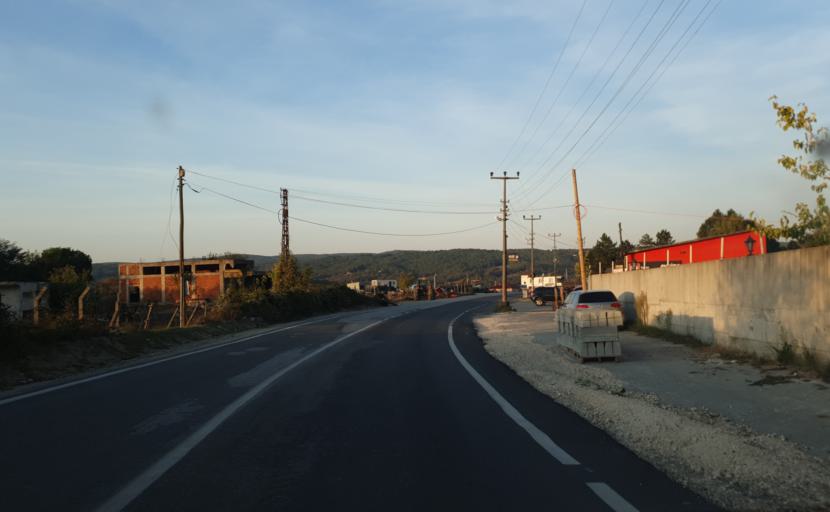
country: TR
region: Kirklareli
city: Sergen
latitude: 41.8277
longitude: 27.7779
